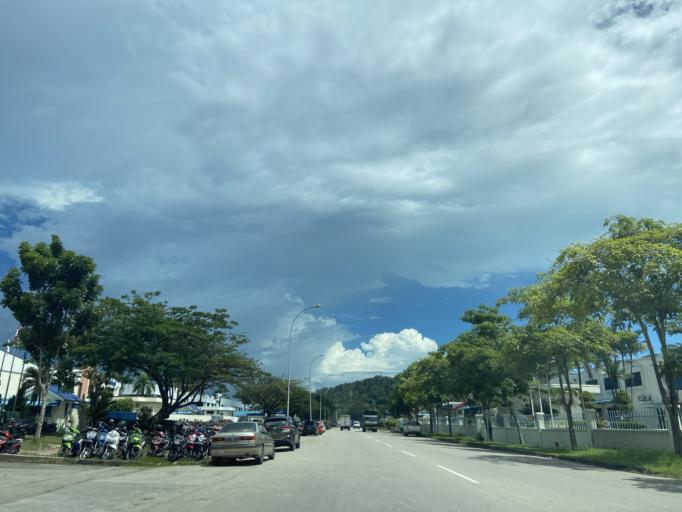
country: SG
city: Singapore
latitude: 1.0600
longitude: 104.0360
